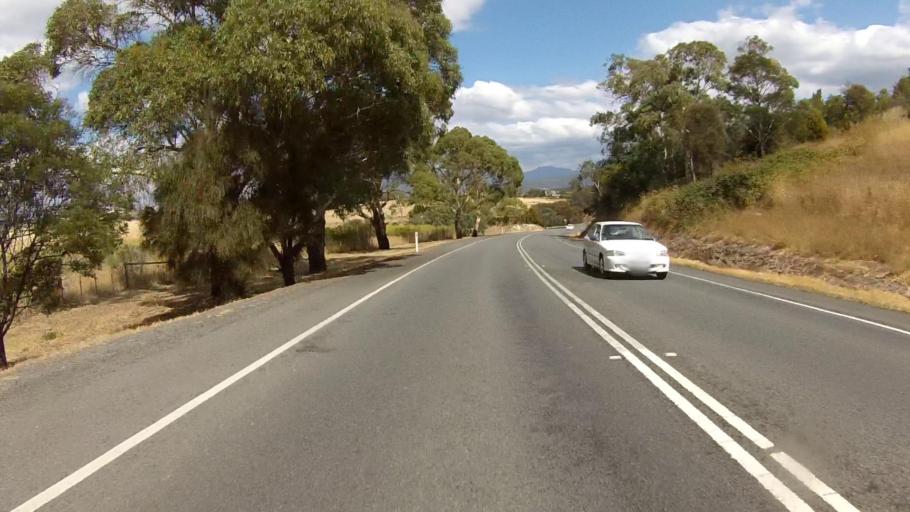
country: AU
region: Tasmania
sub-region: Brighton
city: Old Beach
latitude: -42.7532
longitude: 147.2721
